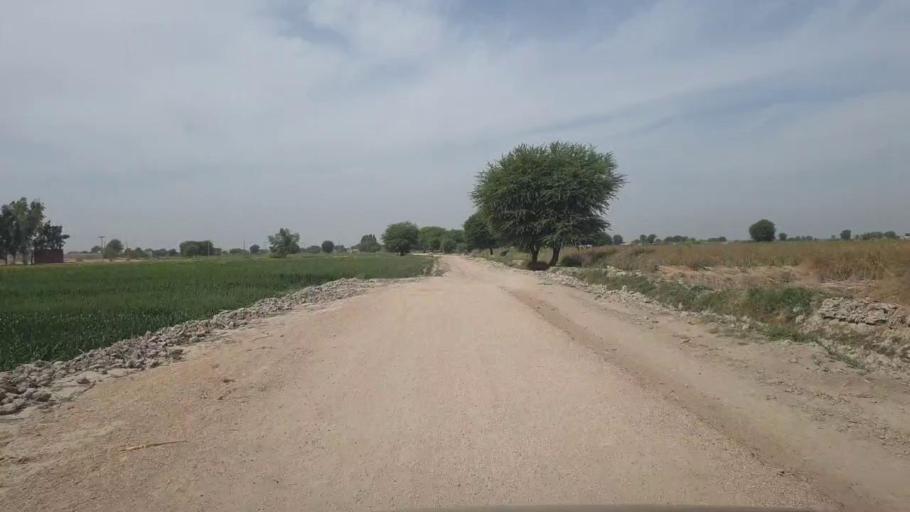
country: PK
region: Sindh
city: Kunri
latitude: 25.2418
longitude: 69.6615
